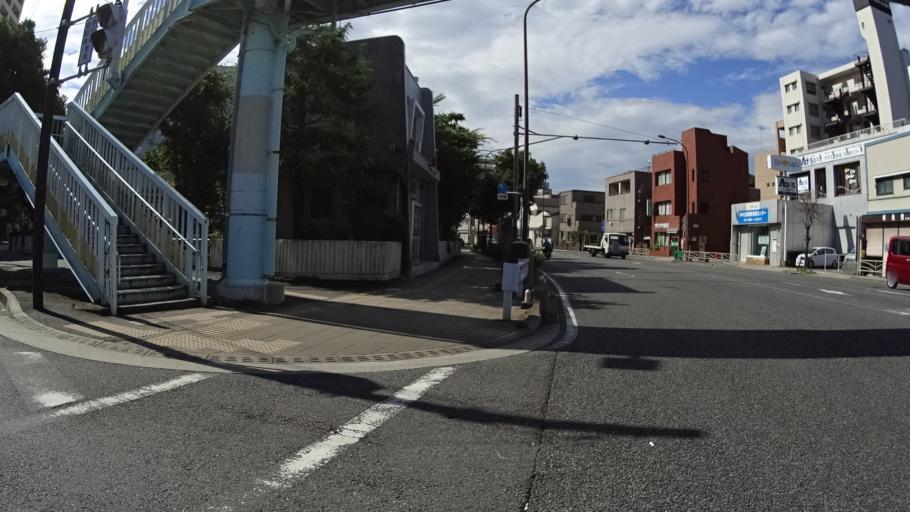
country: JP
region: Kanagawa
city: Yokosuka
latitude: 35.2730
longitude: 139.6770
